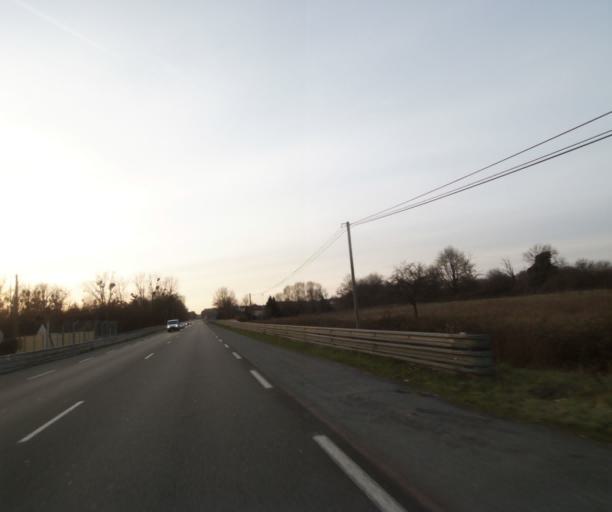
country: FR
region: Pays de la Loire
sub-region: Departement de la Sarthe
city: Ruaudin
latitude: 47.9471
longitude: 0.2322
